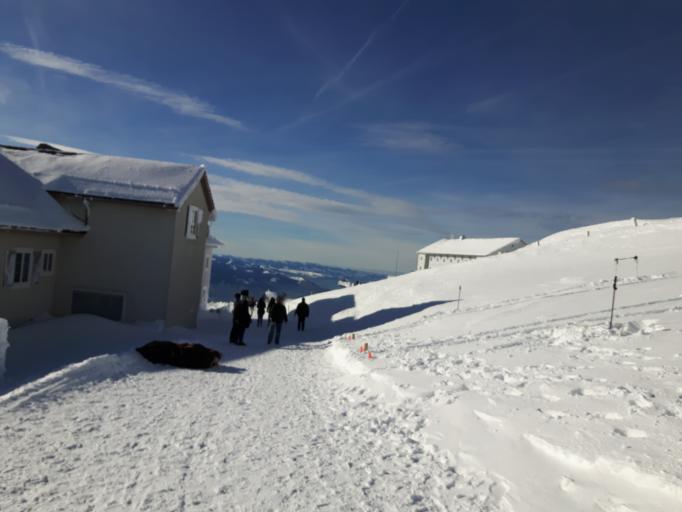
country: CH
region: Schwyz
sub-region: Bezirk Schwyz
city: Arth
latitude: 47.0557
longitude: 8.4860
